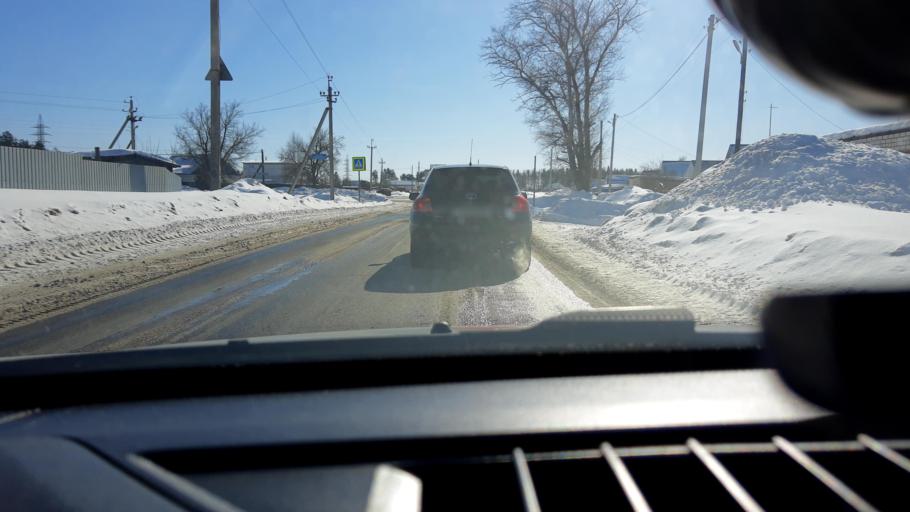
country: RU
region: Nizjnij Novgorod
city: Volodarsk
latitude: 56.2296
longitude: 43.2095
